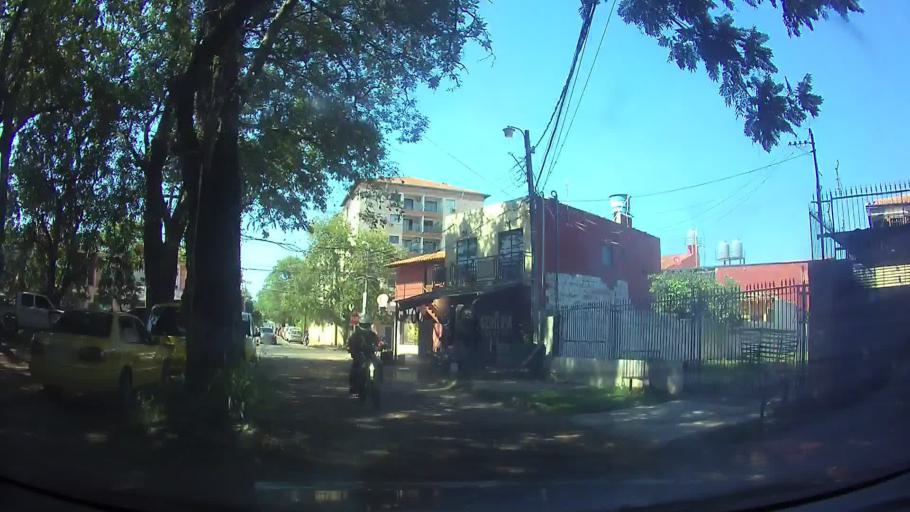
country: PY
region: Central
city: Fernando de la Mora
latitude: -25.3199
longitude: -57.5229
